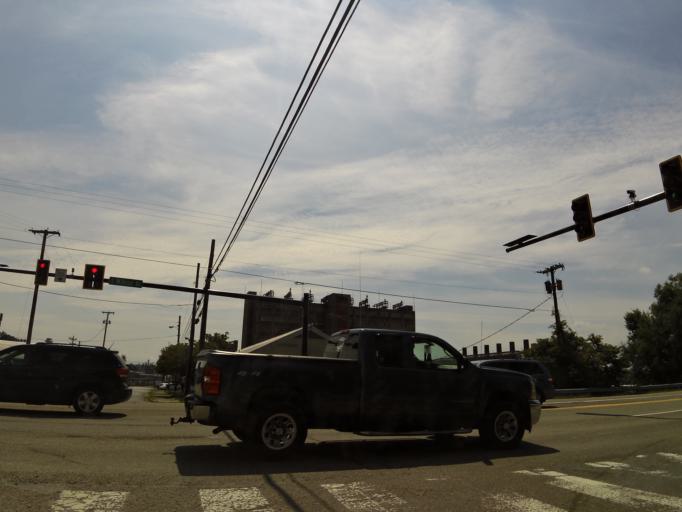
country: US
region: Tennessee
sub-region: Sullivan County
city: Kingsport
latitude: 36.5321
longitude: -82.5528
